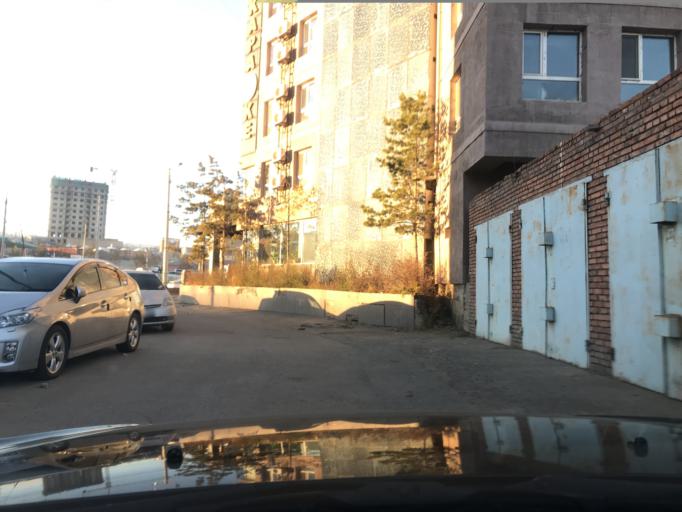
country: MN
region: Ulaanbaatar
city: Ulaanbaatar
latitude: 47.9267
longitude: 106.9042
